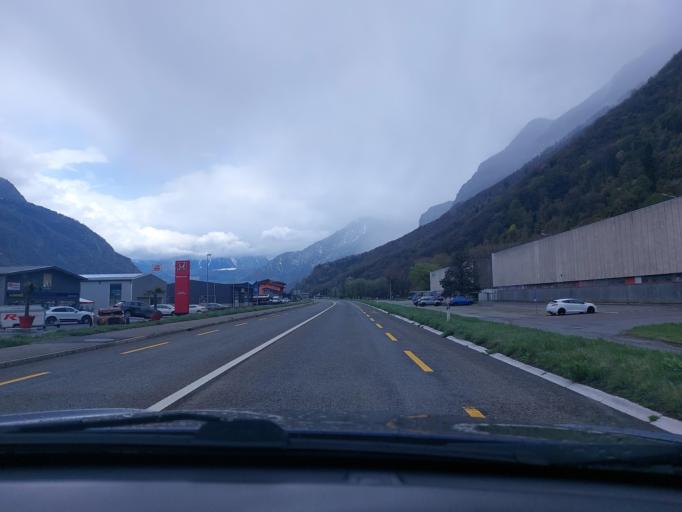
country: CH
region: Valais
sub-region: Martigny District
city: Evionnaz
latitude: 46.1674
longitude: 7.0252
